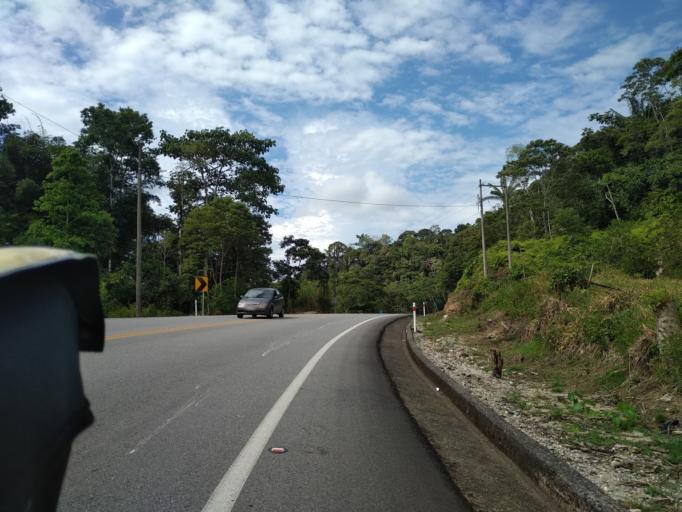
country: EC
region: Napo
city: Tena
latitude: -1.1169
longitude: -77.8100
